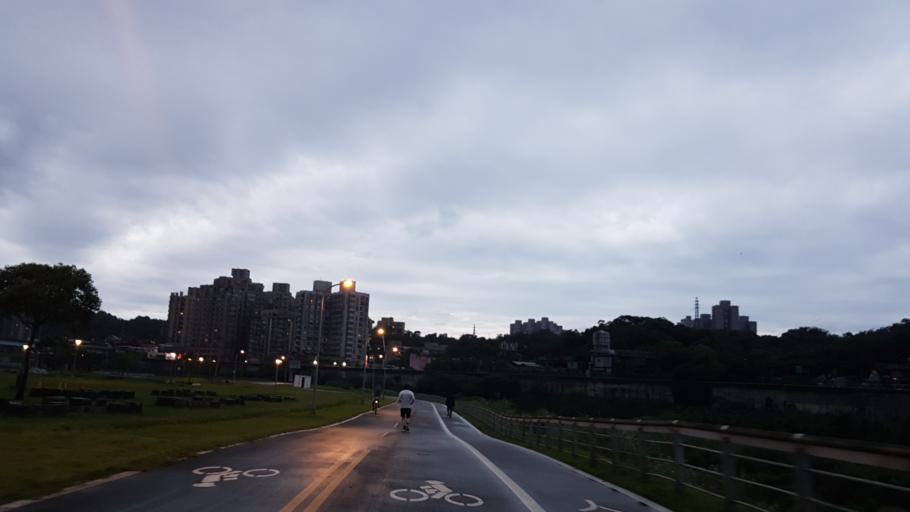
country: TW
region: Taipei
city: Taipei
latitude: 24.9993
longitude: 121.5791
